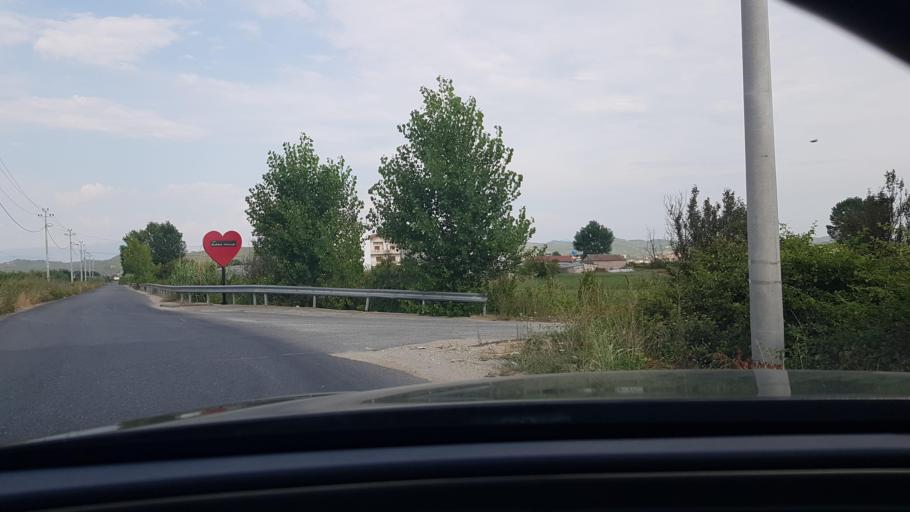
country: AL
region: Durres
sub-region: Rrethi i Durresit
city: Manze
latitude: 41.4720
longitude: 19.5397
